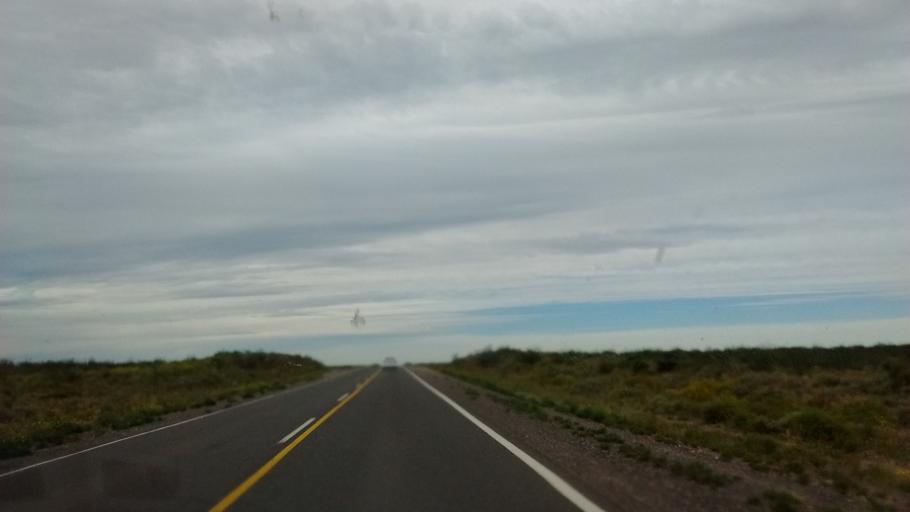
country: AR
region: Rio Negro
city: Catriel
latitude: -38.2819
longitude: -67.9956
